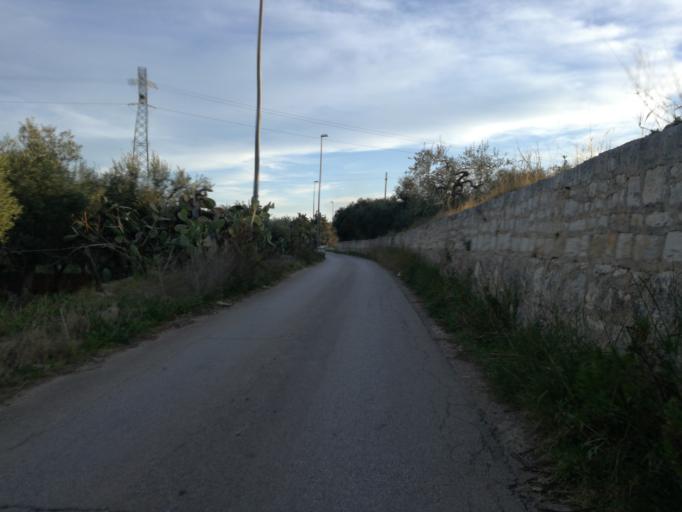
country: IT
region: Apulia
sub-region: Provincia di Bari
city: Lamie
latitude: 41.0367
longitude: 16.8808
